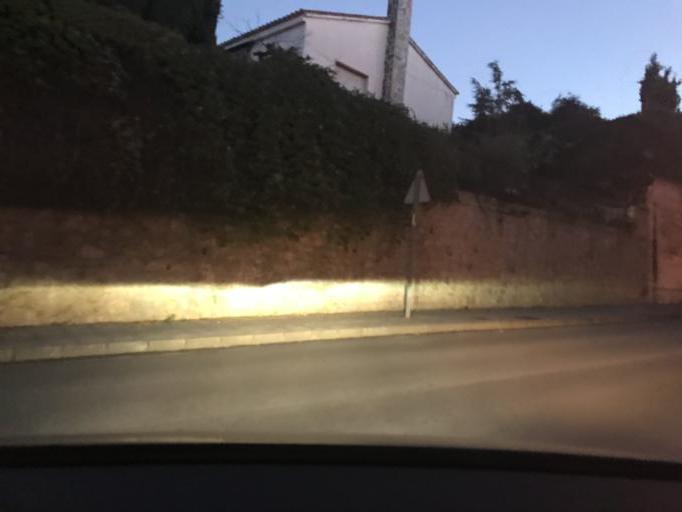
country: ES
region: Andalusia
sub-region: Provincia de Granada
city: Gojar
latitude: 37.1080
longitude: -3.6039
